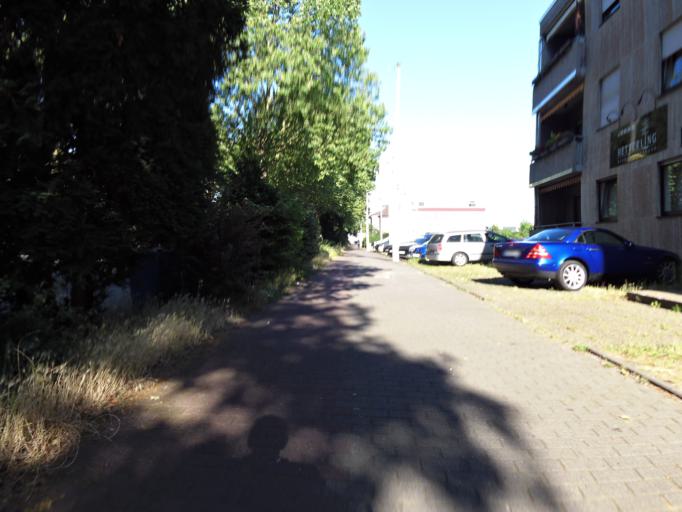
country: DE
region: Rheinland-Pfalz
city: Gartenstadt
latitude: 49.4879
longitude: 8.3929
